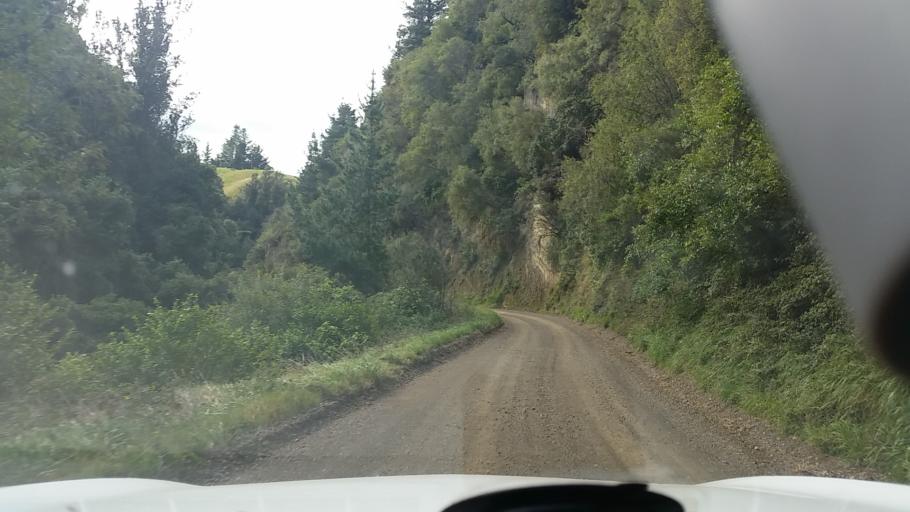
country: NZ
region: Hawke's Bay
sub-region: Napier City
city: Napier
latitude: -39.0941
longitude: 176.8688
